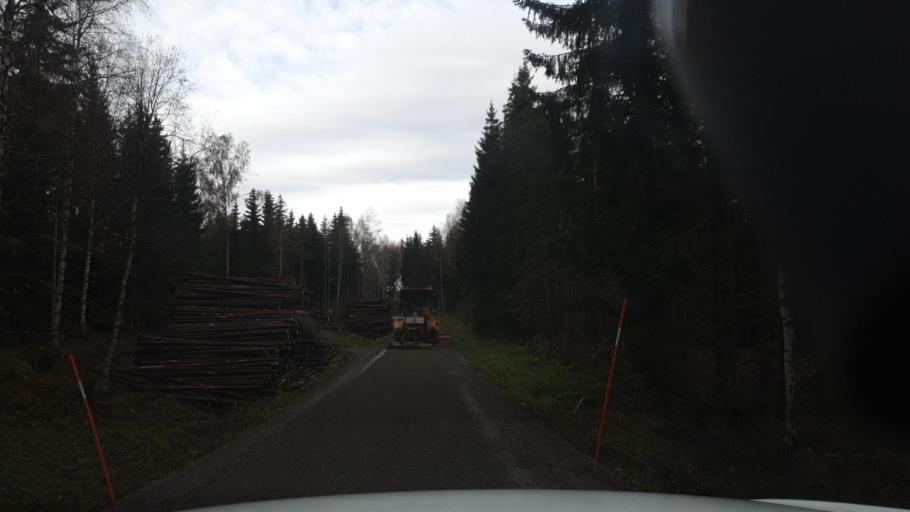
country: SE
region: Vaermland
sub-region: Eda Kommun
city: Amotfors
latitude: 59.8576
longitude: 12.5099
